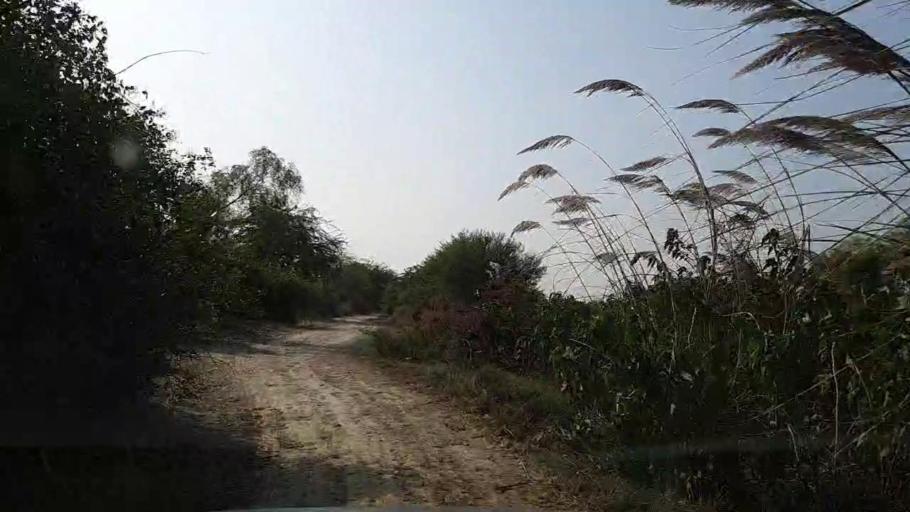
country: PK
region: Sindh
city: Mirpur Sakro
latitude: 24.5754
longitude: 67.5823
